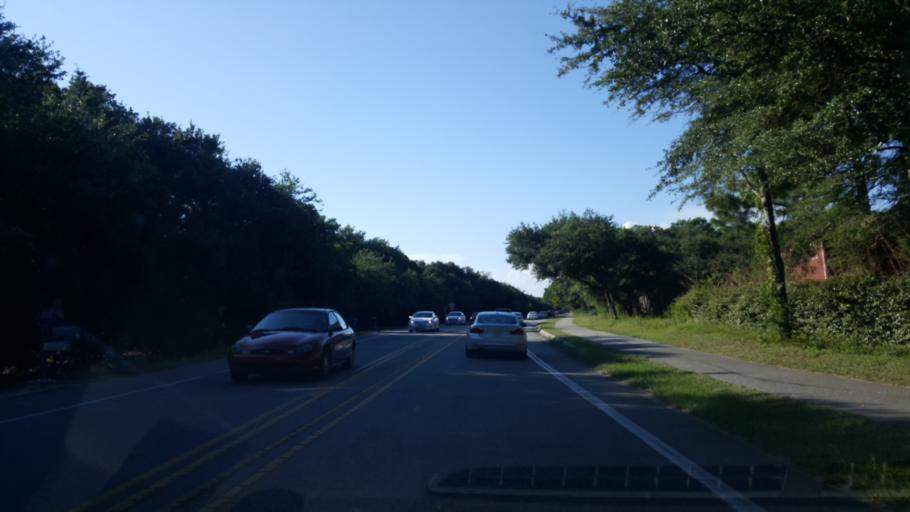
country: US
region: North Carolina
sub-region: Dare County
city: Southern Shores
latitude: 36.1338
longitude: -75.7347
